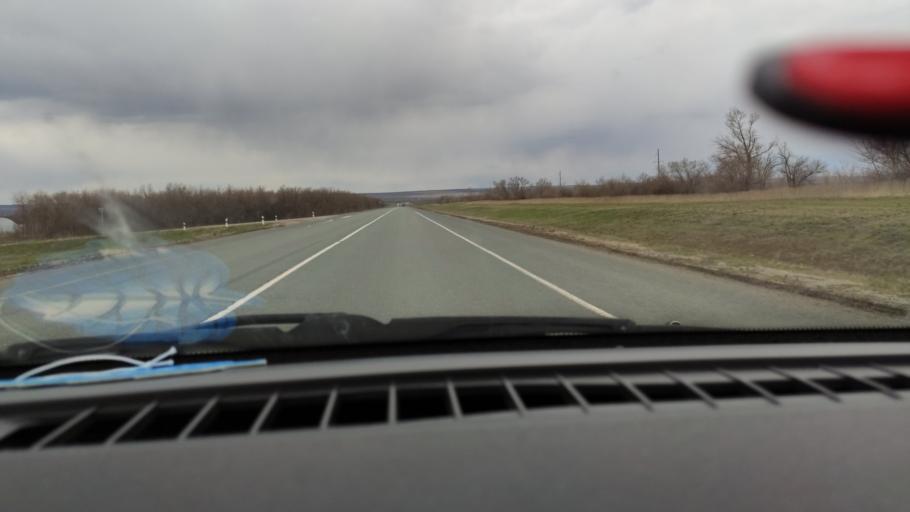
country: RU
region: Saratov
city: Yelshanka
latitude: 51.8268
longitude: 46.2761
